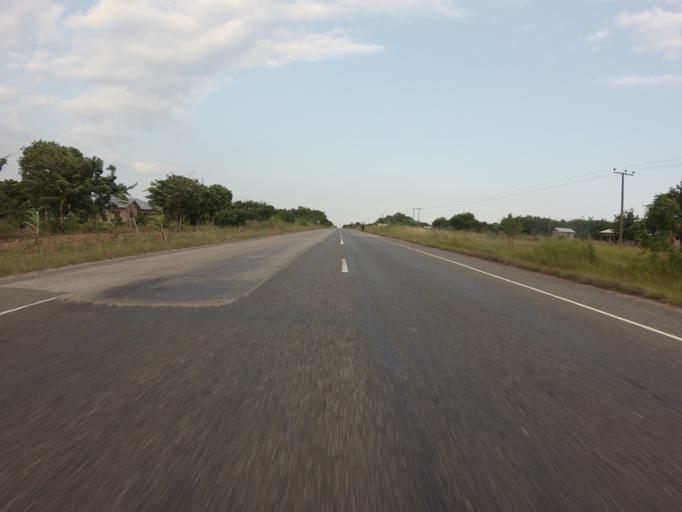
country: GH
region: Volta
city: Anloga
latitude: 6.0878
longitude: 0.5421
